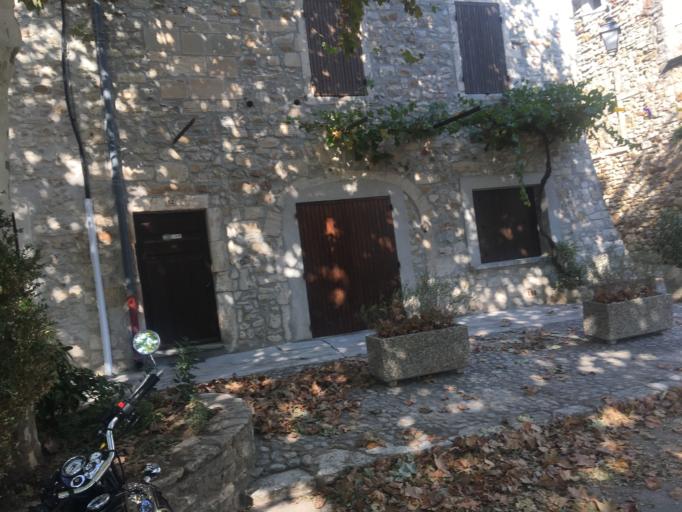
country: FR
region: Languedoc-Roussillon
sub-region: Departement du Gard
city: Saint-Julien-de-Peyrolas
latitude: 44.3028
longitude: 4.5562
